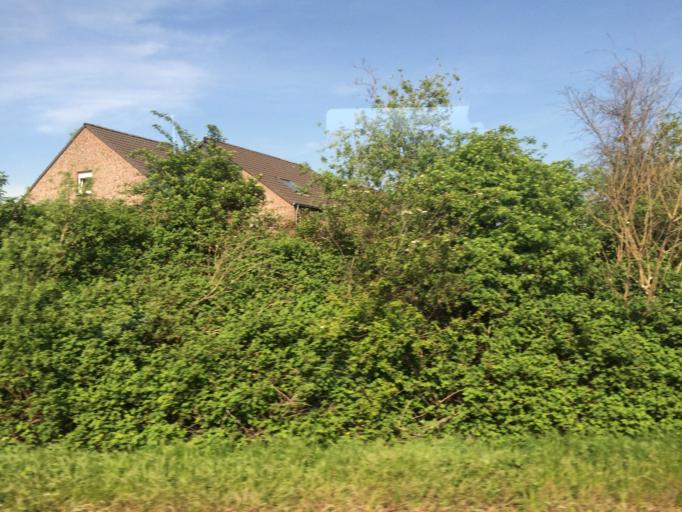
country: DE
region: North Rhine-Westphalia
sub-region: Regierungsbezirk Dusseldorf
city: Langenfeld
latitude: 51.1068
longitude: 6.9348
